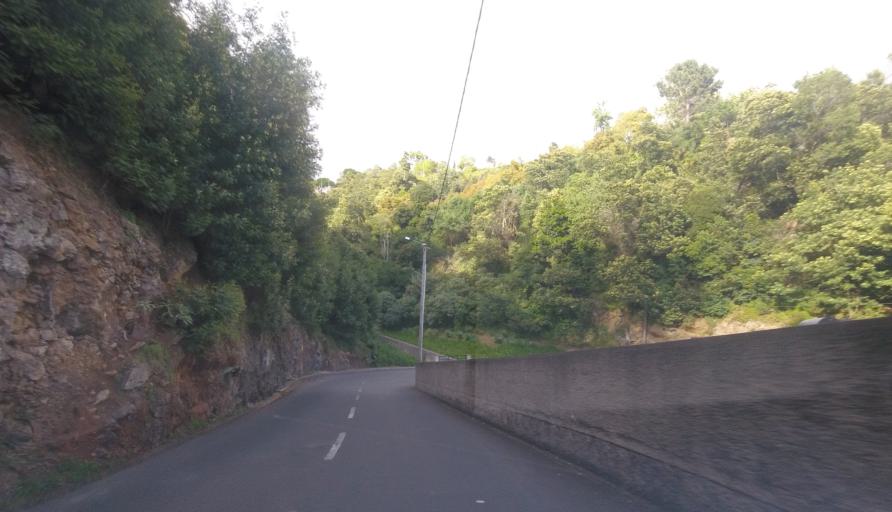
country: PT
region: Madeira
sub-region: Funchal
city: Nossa Senhora do Monte
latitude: 32.6713
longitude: -16.9063
